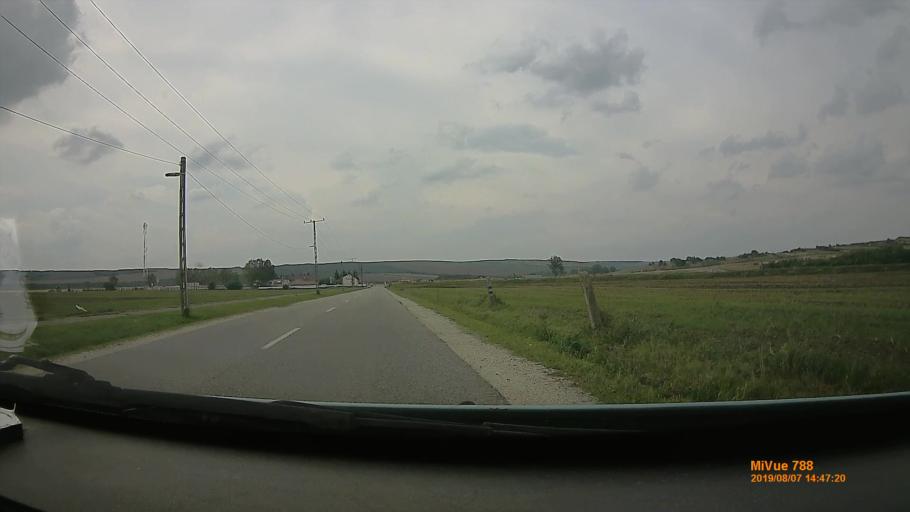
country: HU
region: Borsod-Abauj-Zemplen
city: Halmaj
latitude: 48.2502
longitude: 20.9868
